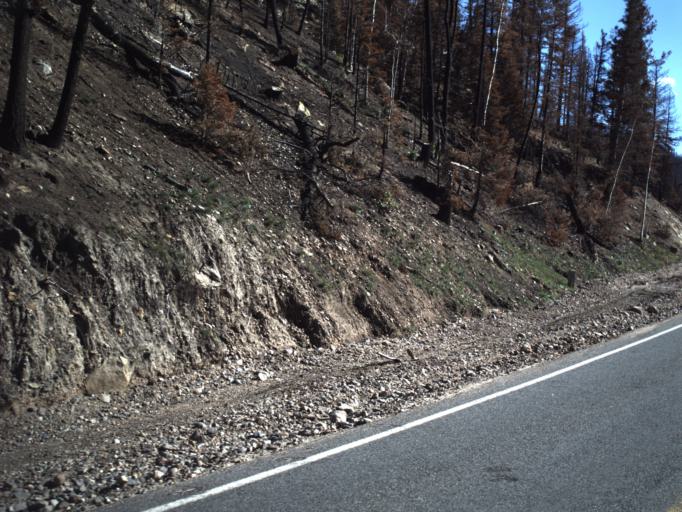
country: US
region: Utah
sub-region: Iron County
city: Parowan
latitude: 37.7461
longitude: -112.8382
